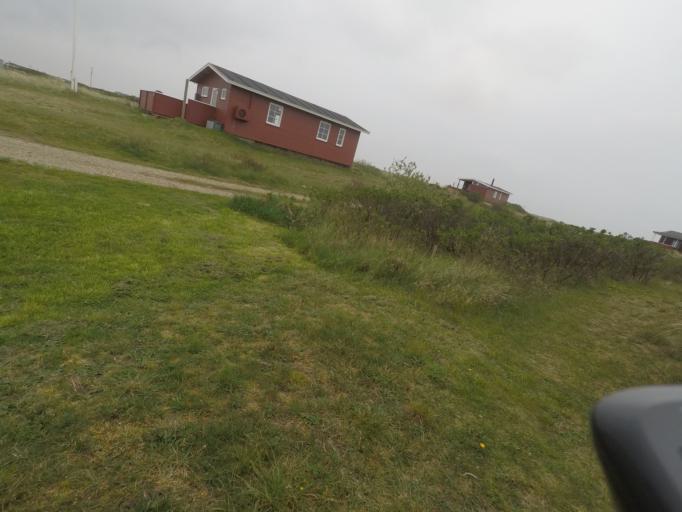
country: DE
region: Schleswig-Holstein
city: List
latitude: 55.1505
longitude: 8.4992
